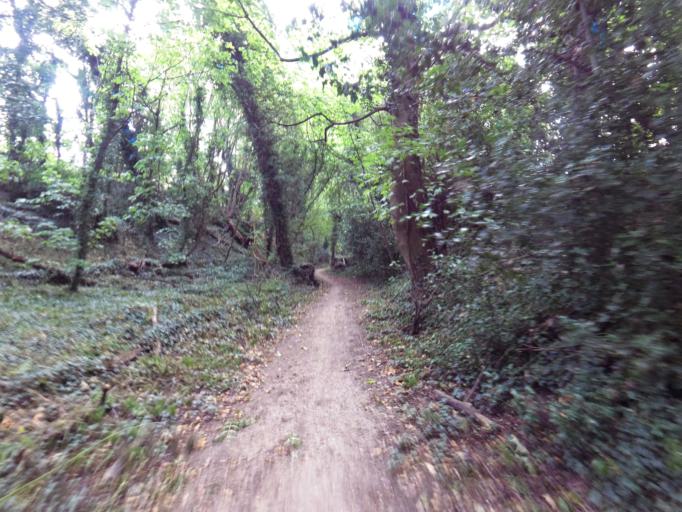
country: GB
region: England
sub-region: Hertfordshire
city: Shenley AV
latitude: 51.7111
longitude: -0.2644
